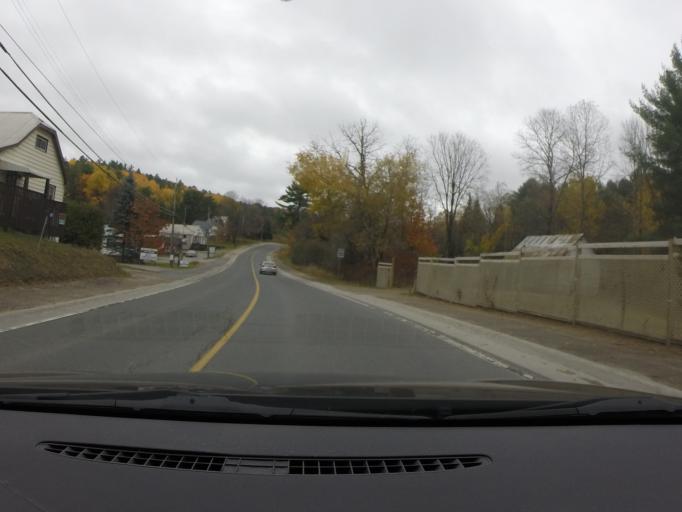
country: CA
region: Ontario
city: Bancroft
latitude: 45.0589
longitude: -77.8443
